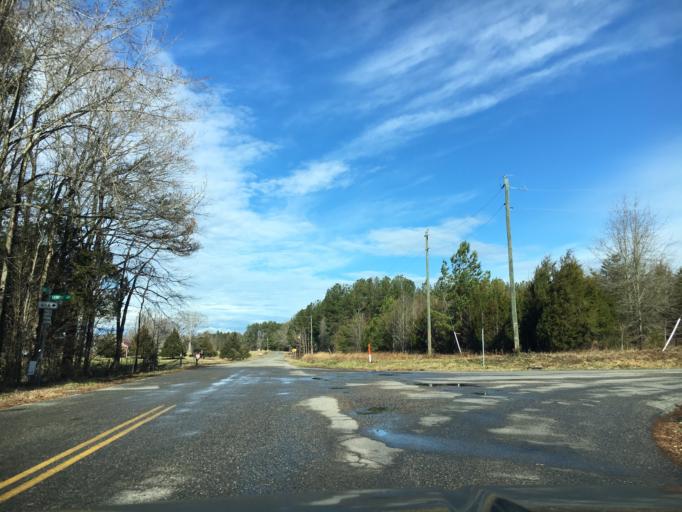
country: US
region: Virginia
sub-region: Amelia County
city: Amelia Court House
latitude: 37.3893
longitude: -78.1211
